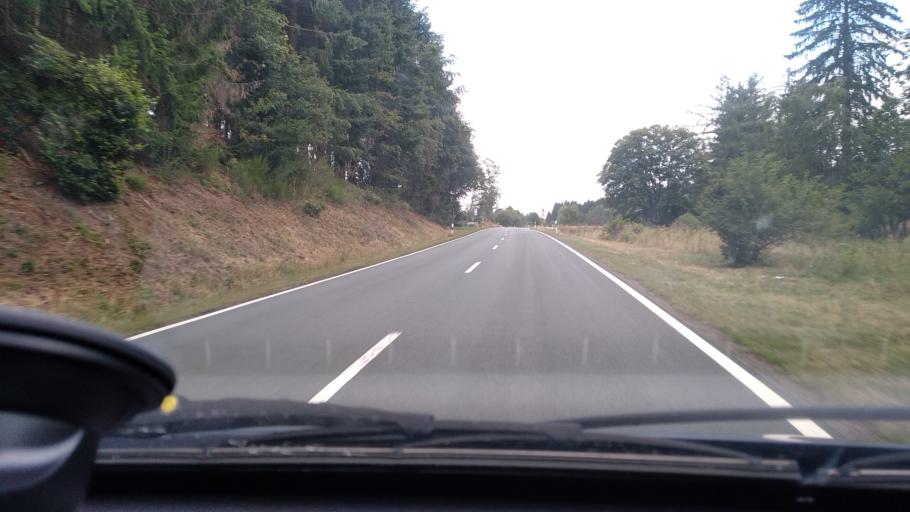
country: DE
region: Hesse
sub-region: Regierungsbezirk Giessen
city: Siegbach
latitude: 50.7893
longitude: 8.3657
